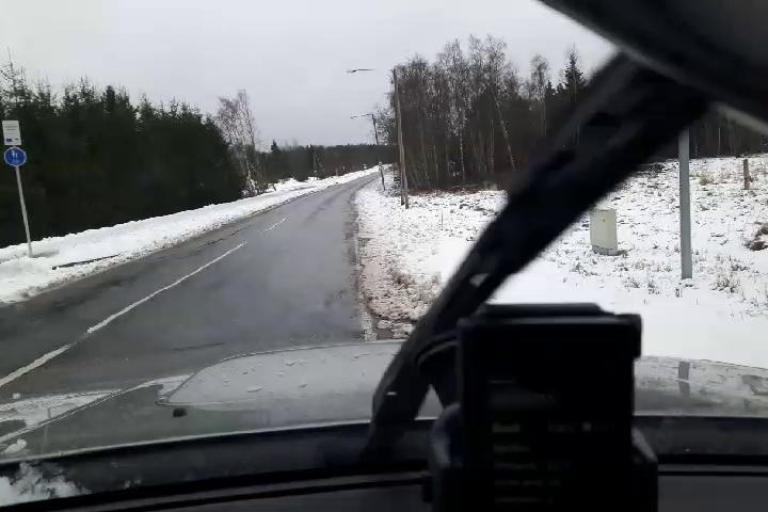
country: EE
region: Harju
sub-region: Harku vald
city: Tabasalu
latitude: 59.4379
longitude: 24.4995
